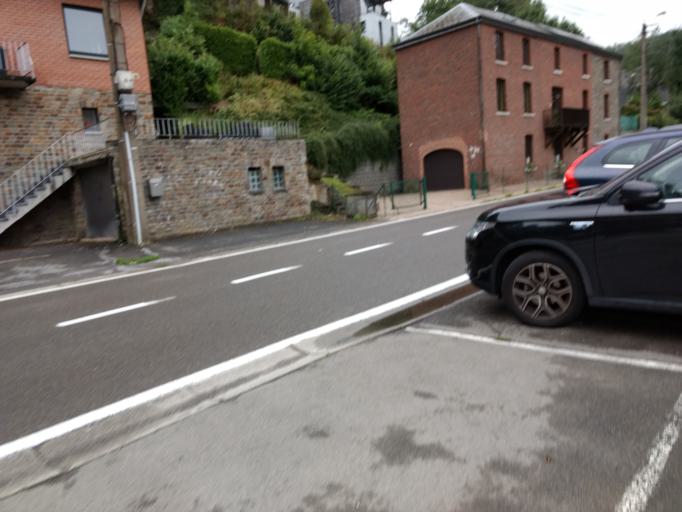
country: BE
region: Wallonia
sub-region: Province du Luxembourg
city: La Roche-en-Ardenne
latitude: 50.1794
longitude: 5.5838
